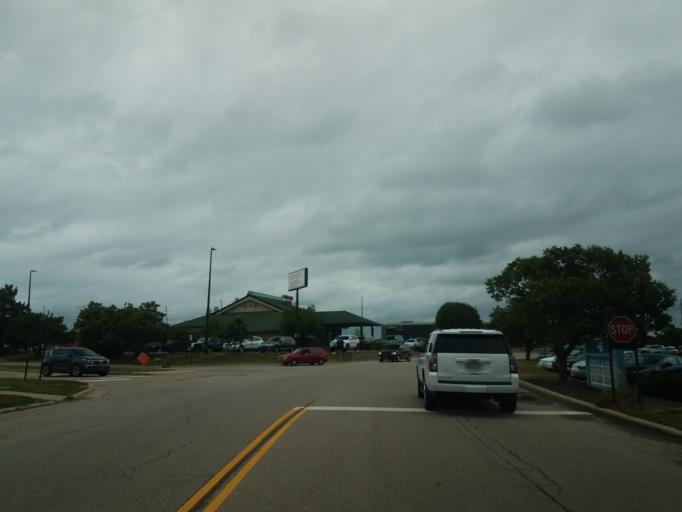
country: US
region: Illinois
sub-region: McLean County
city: Normal
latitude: 40.5088
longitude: -88.9560
